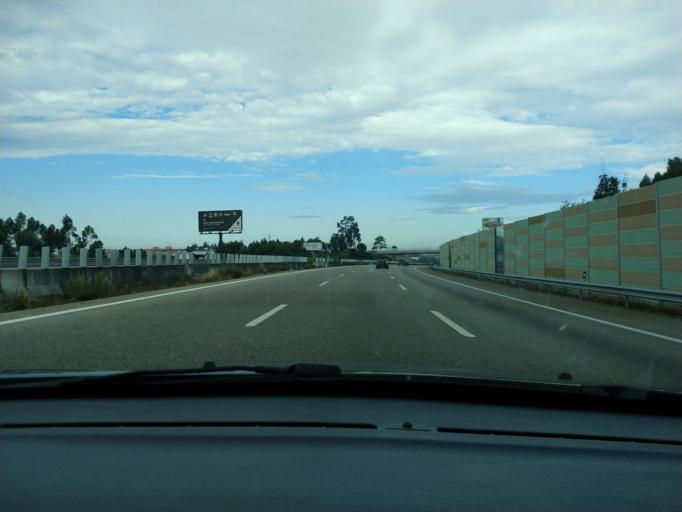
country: PT
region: Aveiro
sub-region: Santa Maria da Feira
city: Rio Meao
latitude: 40.9690
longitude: -8.5705
